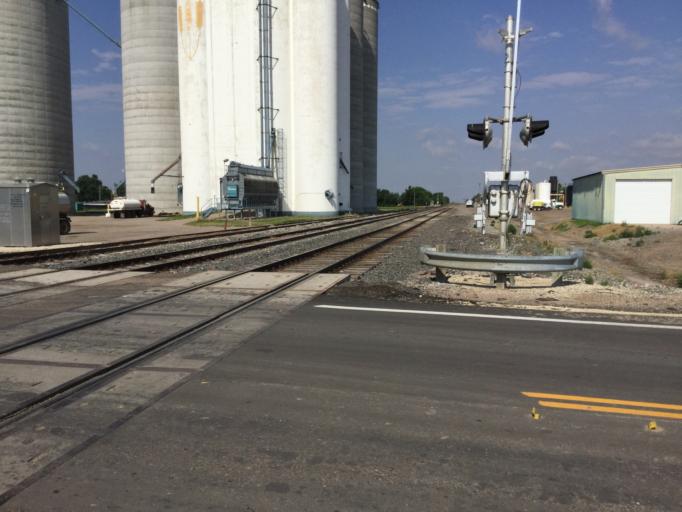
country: US
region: Kansas
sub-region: Pawnee County
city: Larned
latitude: 37.9531
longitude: -99.0955
